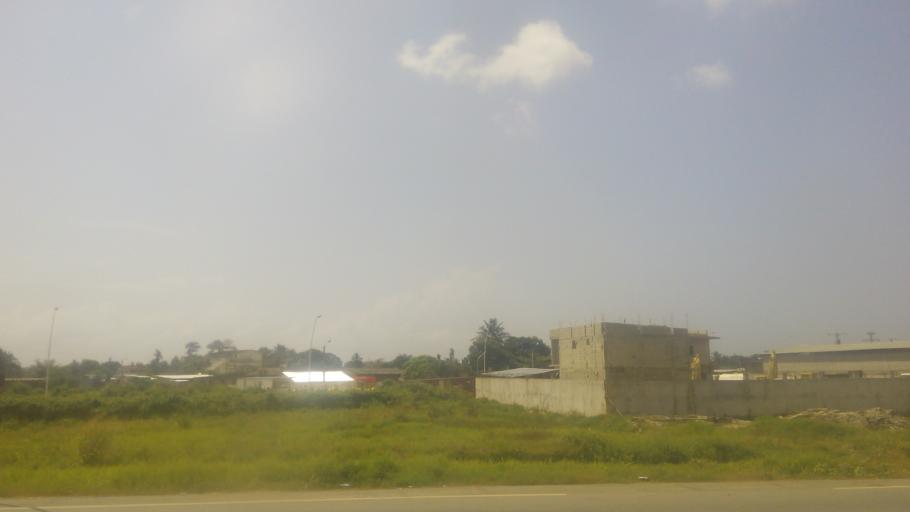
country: CI
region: Sud-Comoe
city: Grand-Bassam
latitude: 5.2232
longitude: -3.7271
